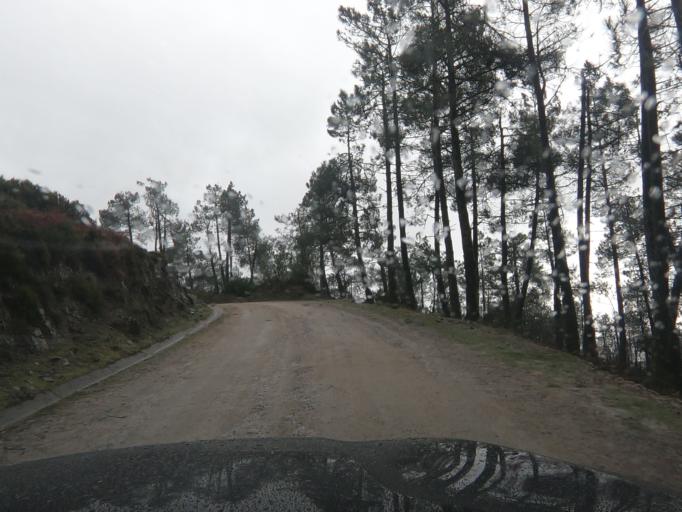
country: PT
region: Vila Real
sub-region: Mondim de Basto
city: Mondim de Basto
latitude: 41.3223
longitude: -7.8695
